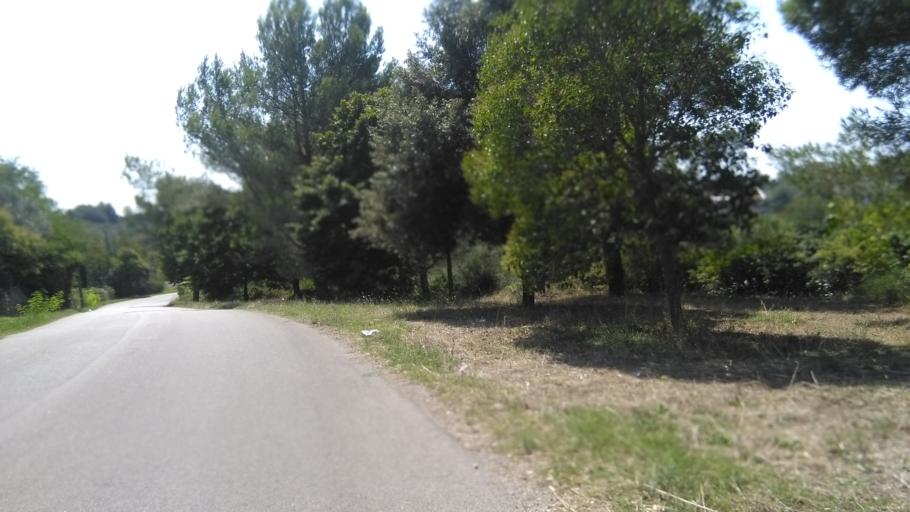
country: IT
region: Apulia
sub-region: Provincia di Bari
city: Putignano
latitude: 40.8355
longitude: 17.1327
